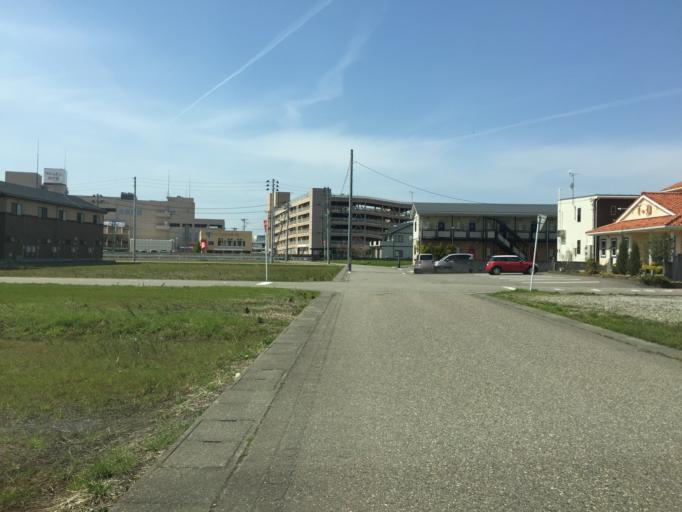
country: JP
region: Niigata
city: Tsubame
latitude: 37.6530
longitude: 138.9367
